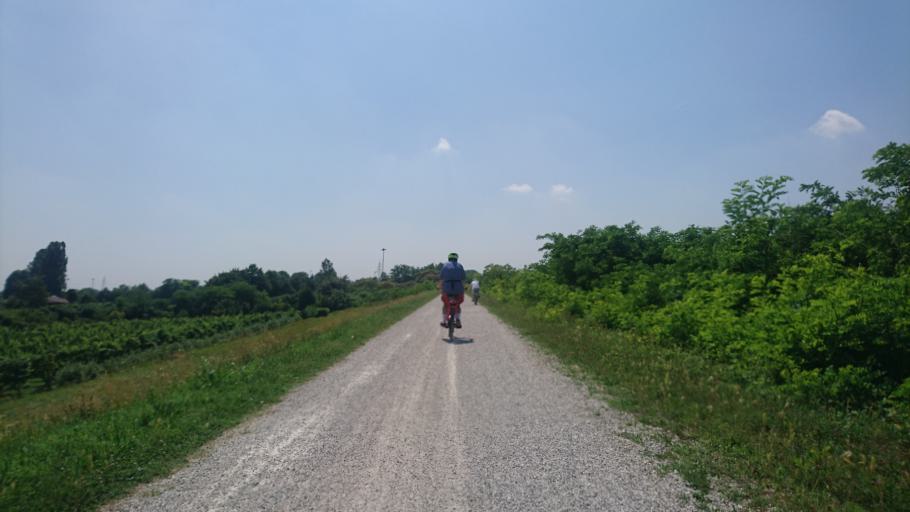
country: IT
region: Veneto
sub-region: Provincia di Venezia
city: Galta
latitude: 45.3882
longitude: 12.0156
